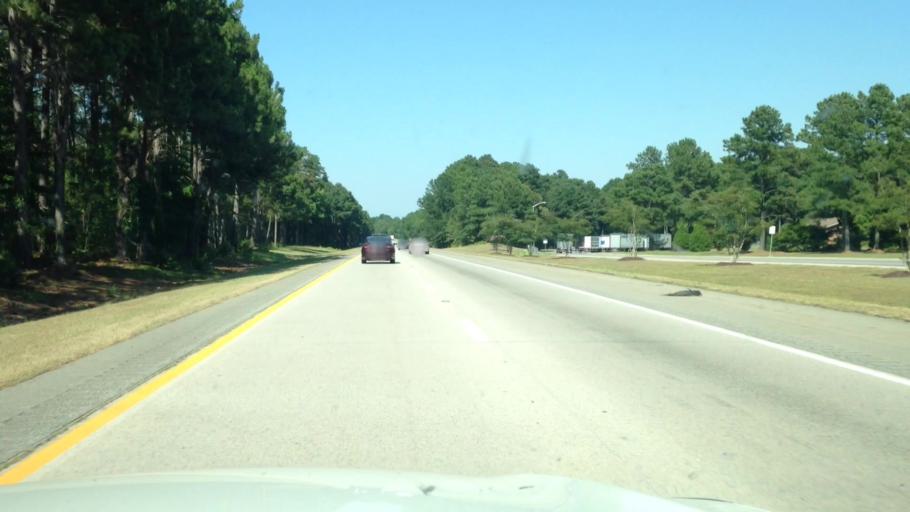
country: US
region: North Carolina
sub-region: Nash County
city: Red Oak
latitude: 36.0255
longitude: -77.8496
